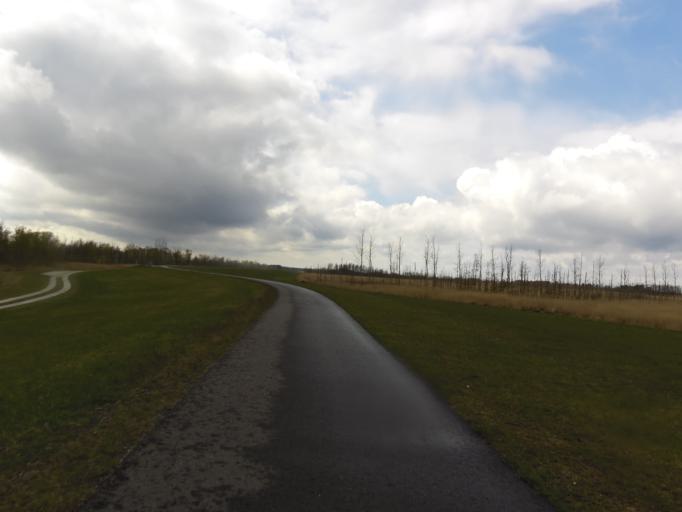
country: DE
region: Mecklenburg-Vorpommern
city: Altenpleen
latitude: 54.4316
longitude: 12.8522
